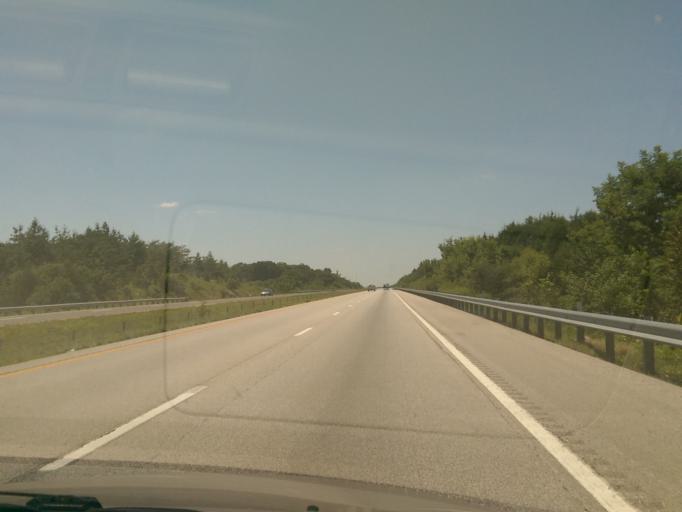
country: US
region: Missouri
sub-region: Cooper County
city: Boonville
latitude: 38.9337
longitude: -92.9602
